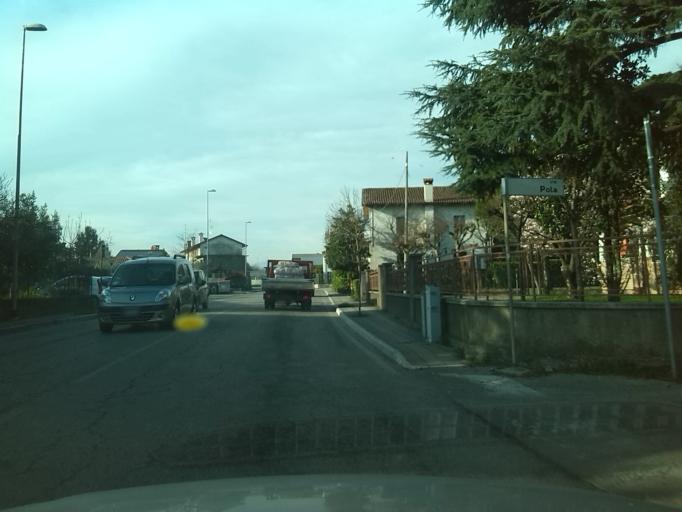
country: IT
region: Friuli Venezia Giulia
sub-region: Provincia di Udine
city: Manzano
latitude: 45.9938
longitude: 13.3919
